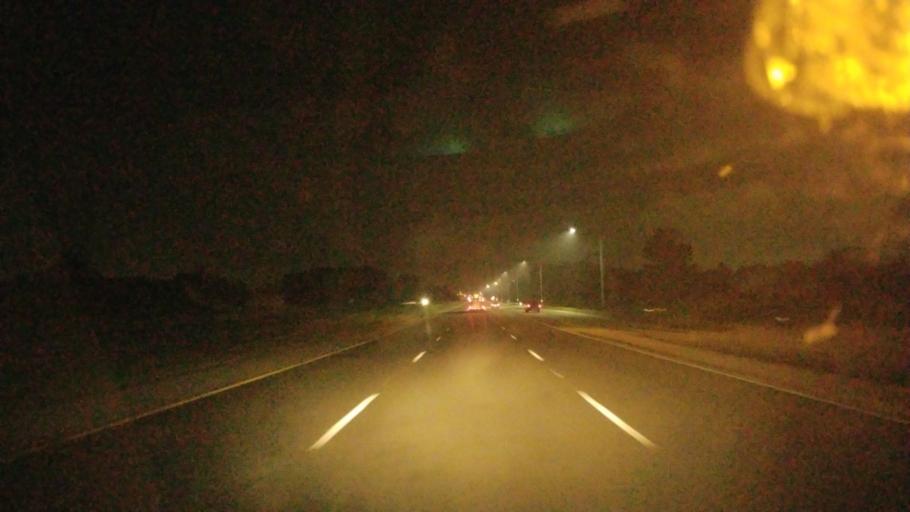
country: US
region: Illinois
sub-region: Madison County
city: Glen Carbon
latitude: 38.7567
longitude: -90.0108
